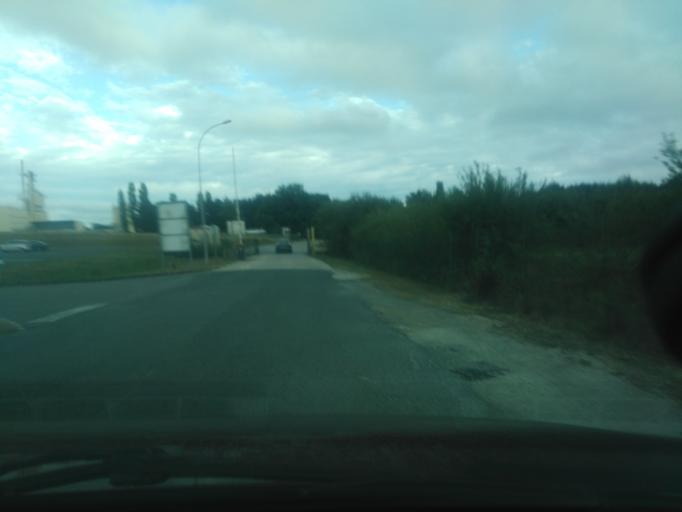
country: FR
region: Pays de la Loire
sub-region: Departement de la Vendee
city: Dompierre-sur-Yon
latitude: 46.6958
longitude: -1.3747
